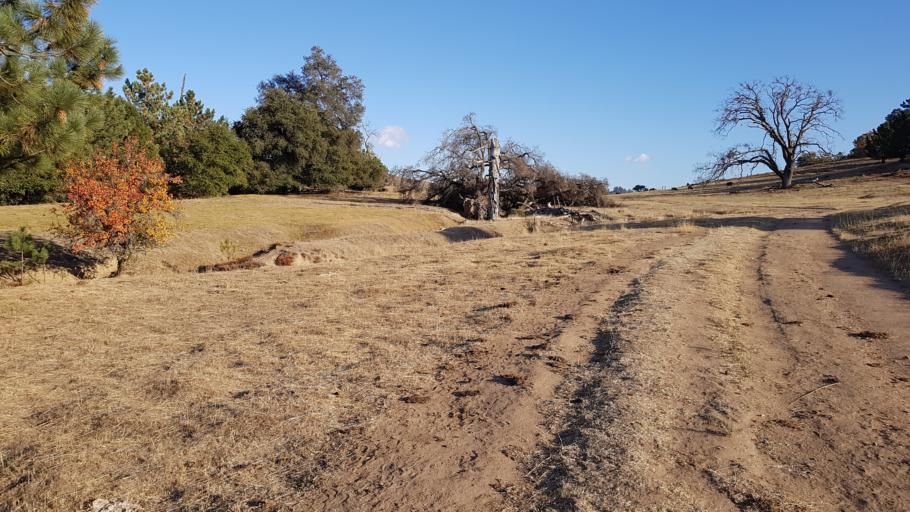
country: US
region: California
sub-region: San Diego County
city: Julian
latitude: 33.1089
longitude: -116.6219
